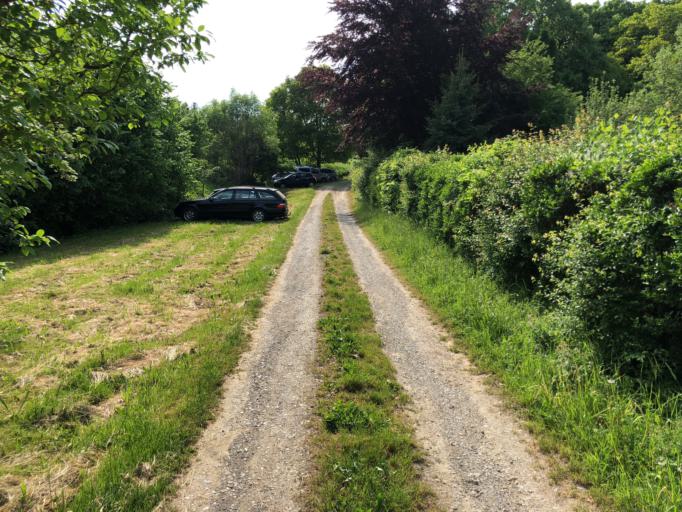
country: DE
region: Baden-Wuerttemberg
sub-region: Tuebingen Region
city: Mossingen
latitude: 48.4051
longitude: 9.0724
